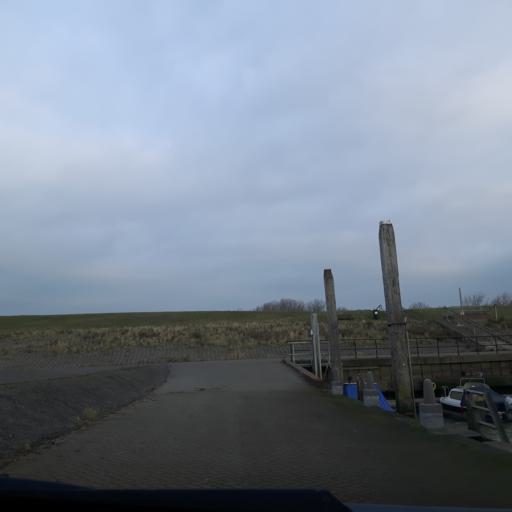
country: NL
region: Zeeland
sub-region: Gemeente Terneuzen
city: Terneuzen
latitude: 51.3857
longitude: 3.8171
